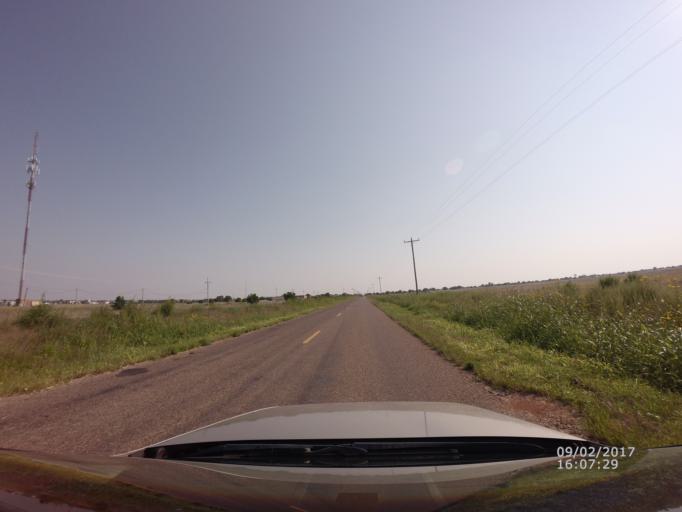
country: US
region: New Mexico
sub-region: Curry County
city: Clovis
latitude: 34.4398
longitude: -103.2141
